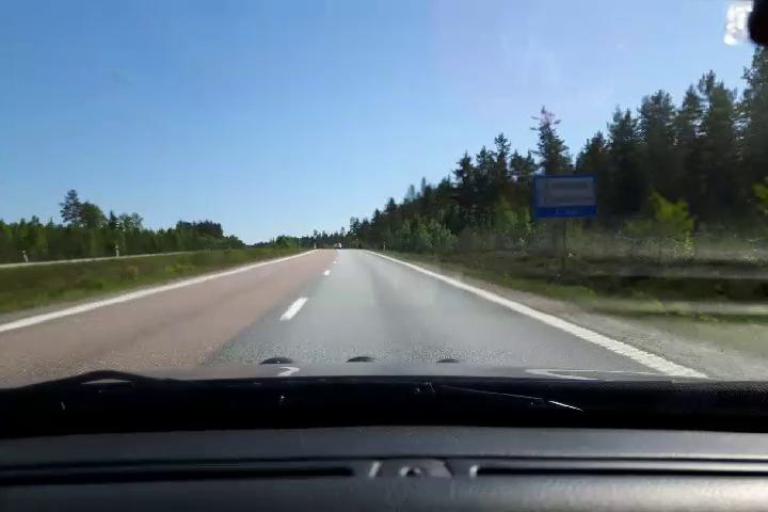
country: SE
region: Gaevleborg
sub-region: Soderhamns Kommun
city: Soderhamn
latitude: 61.4603
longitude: 16.9881
